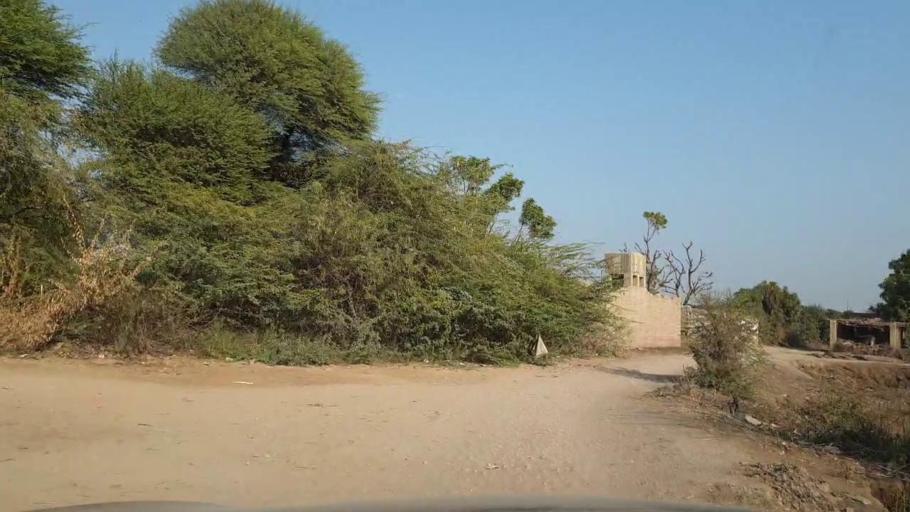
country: PK
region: Sindh
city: Tando Allahyar
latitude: 25.5816
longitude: 68.7643
